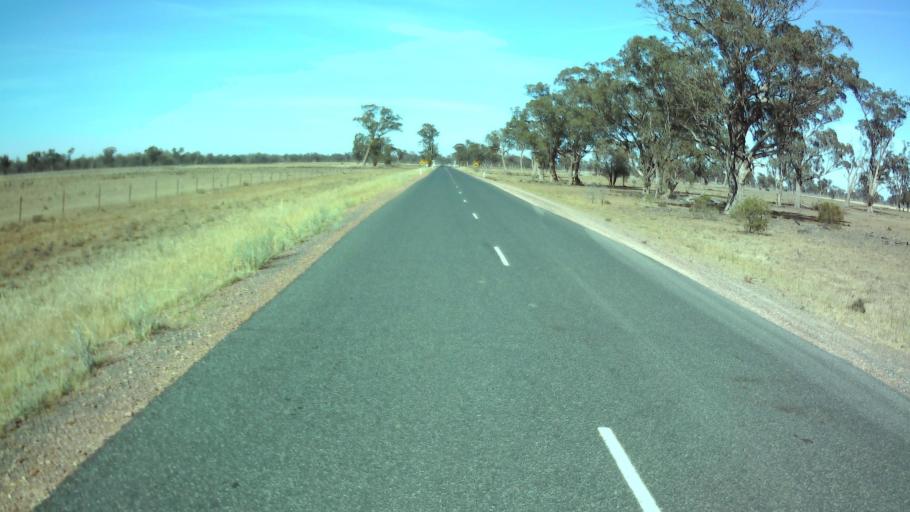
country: AU
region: New South Wales
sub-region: Weddin
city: Grenfell
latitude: -34.1049
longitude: 147.8662
